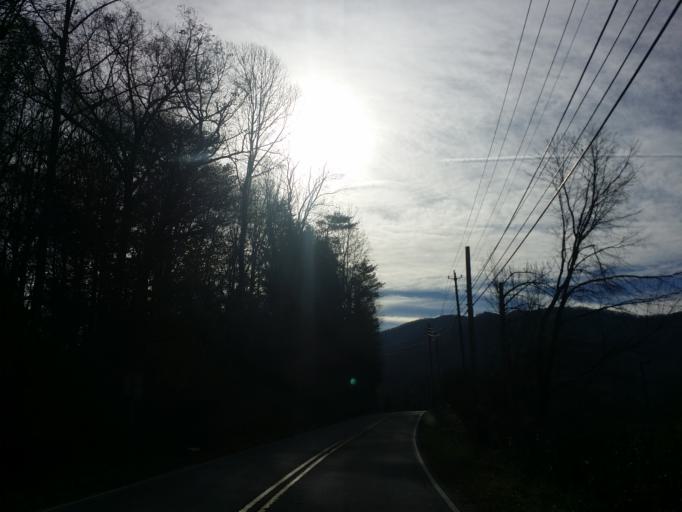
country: US
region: North Carolina
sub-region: Buncombe County
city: Swannanoa
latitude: 35.6061
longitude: -82.4099
